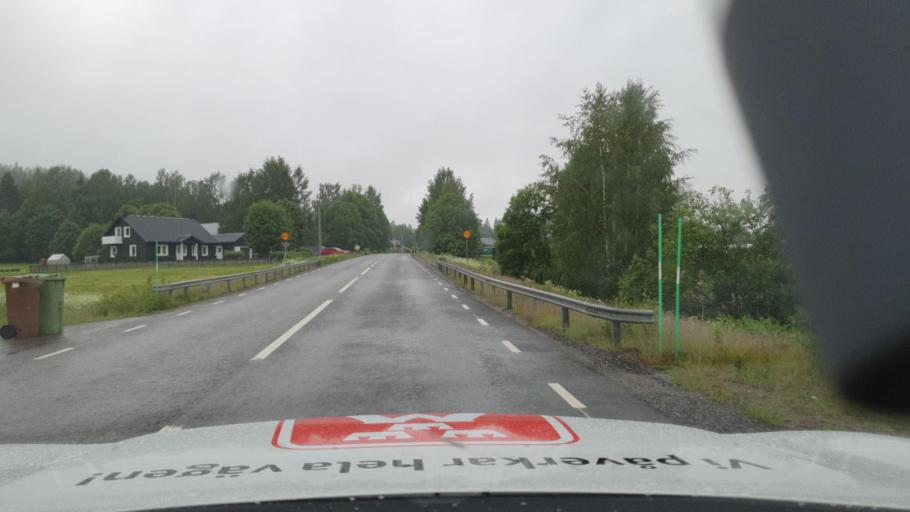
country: SE
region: Vaesterbotten
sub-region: Vannas Kommun
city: Vannasby
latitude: 63.7803
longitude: 19.8441
